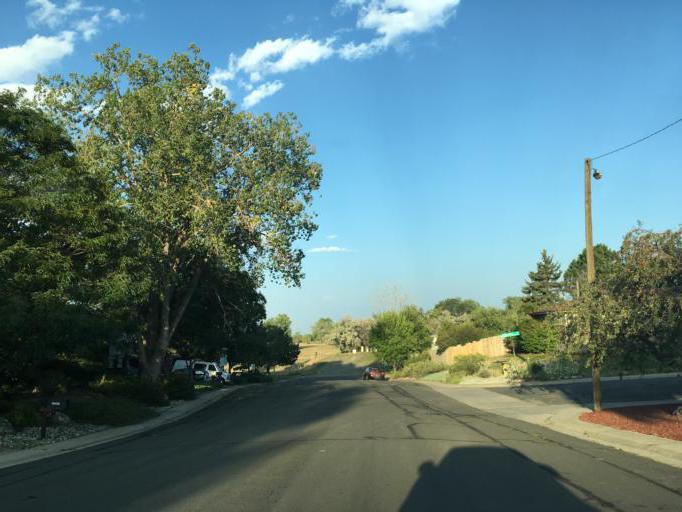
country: US
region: Colorado
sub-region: Jefferson County
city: Applewood
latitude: 39.7944
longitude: -105.1489
